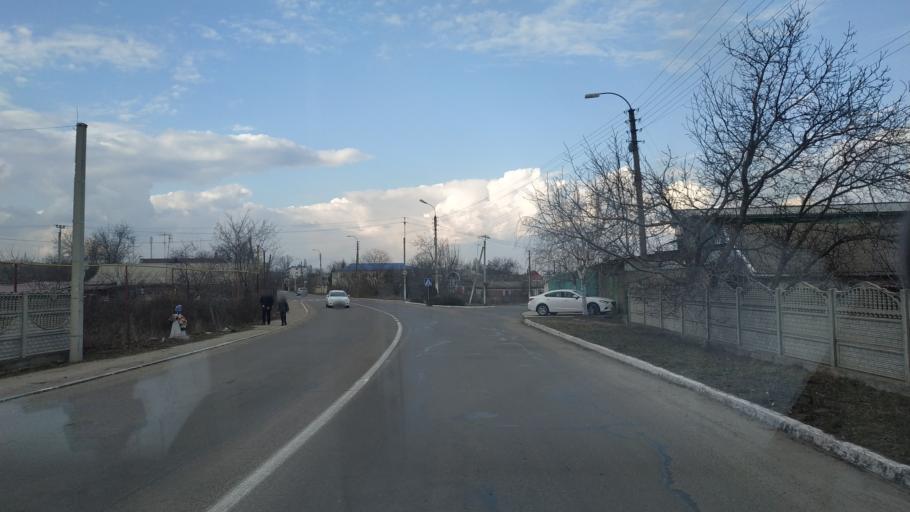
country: MD
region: Anenii Noi
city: Varnita
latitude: 46.8575
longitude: 29.4795
